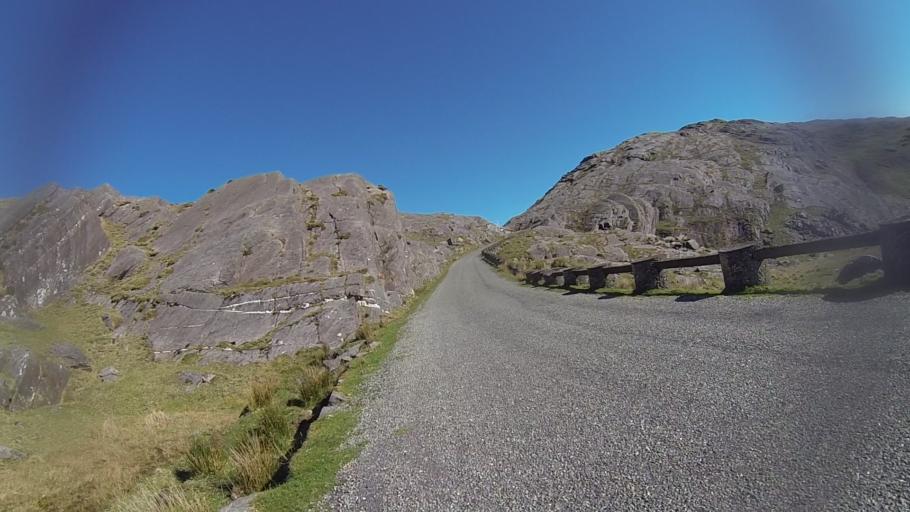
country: IE
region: Munster
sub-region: Ciarrai
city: Kenmare
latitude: 51.7197
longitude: -9.7569
